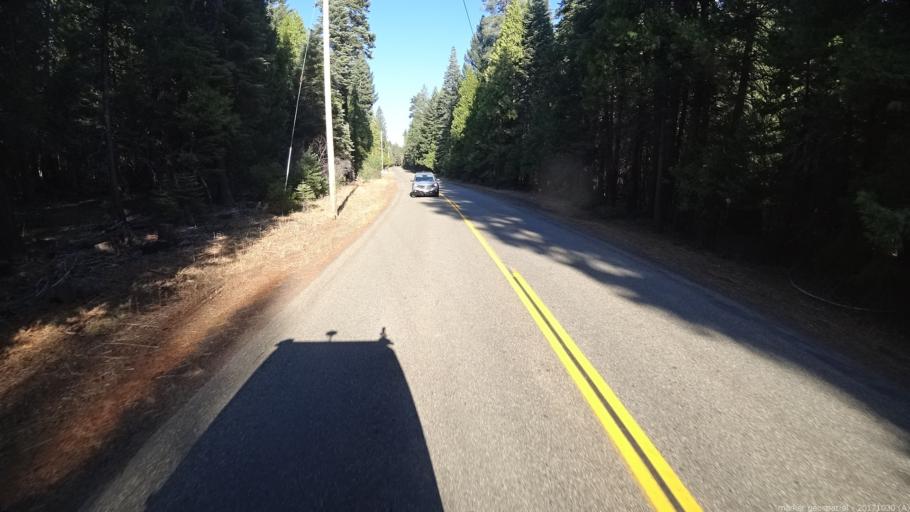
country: US
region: California
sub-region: Shasta County
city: Shingletown
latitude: 40.5182
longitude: -121.7548
